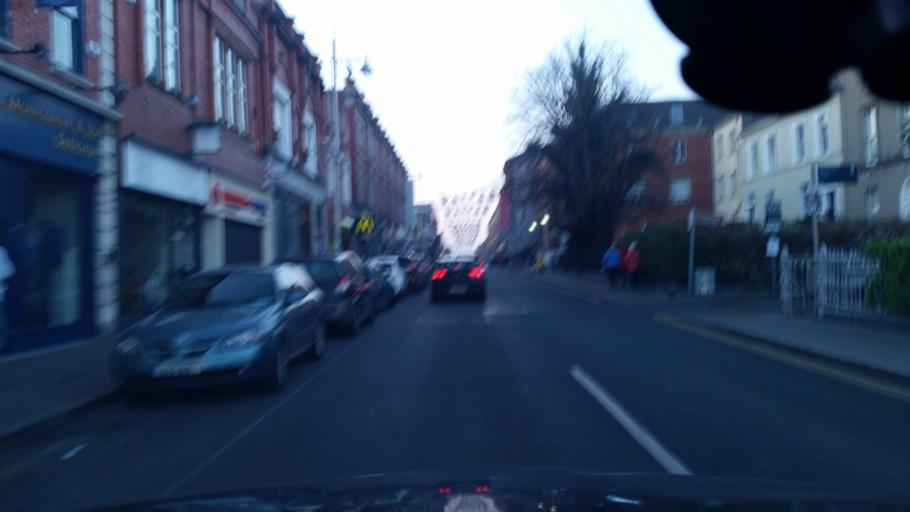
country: IE
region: Leinster
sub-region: Dun Laoghaire-Rathdown
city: Dun Laoghaire
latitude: 53.2911
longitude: -6.1333
